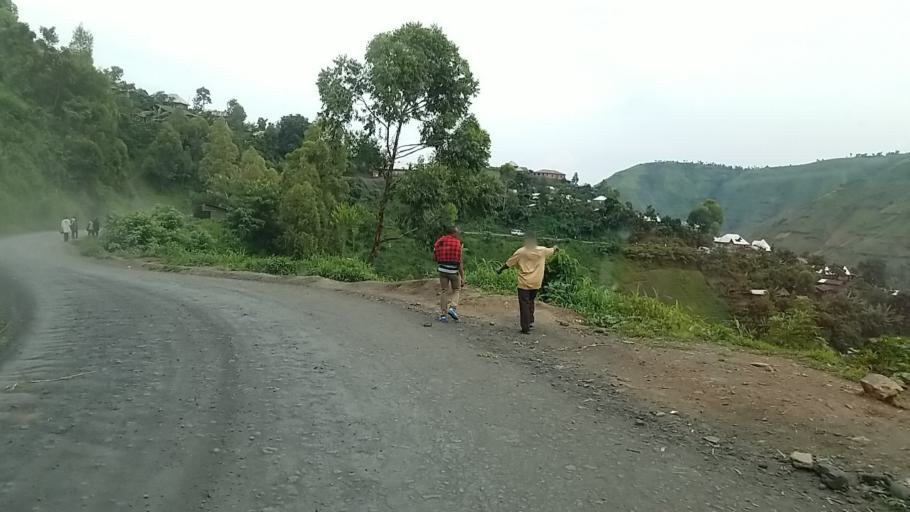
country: CD
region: Nord Kivu
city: Sake
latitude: -1.7578
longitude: 28.9852
